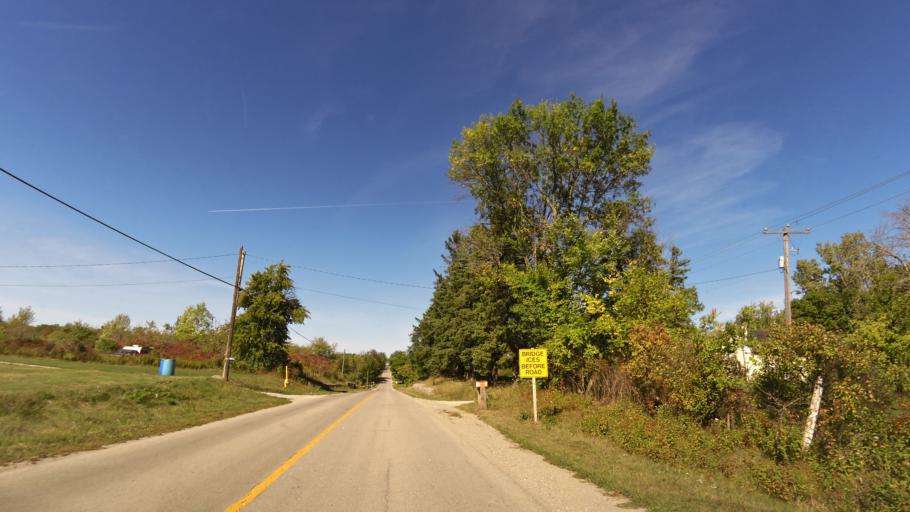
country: CA
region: Ontario
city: Ancaster
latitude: 43.0138
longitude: -80.0249
